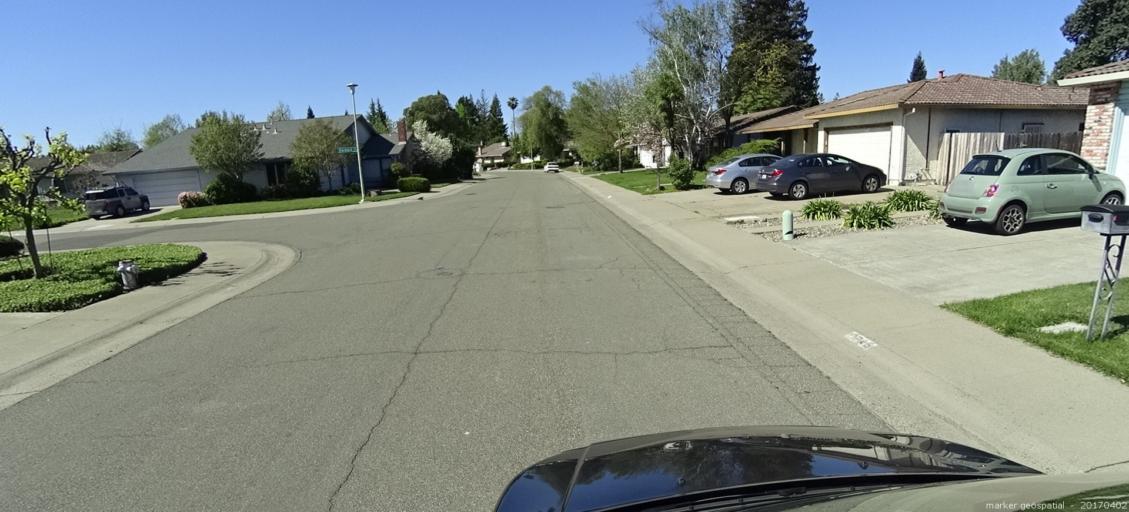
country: US
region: California
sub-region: Yolo County
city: West Sacramento
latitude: 38.5044
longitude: -121.5429
